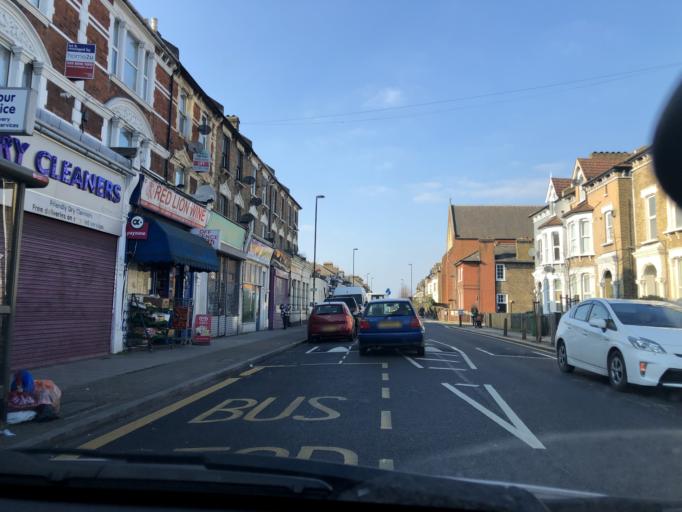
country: GB
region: England
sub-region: Greater London
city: Catford
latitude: 51.4514
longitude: -0.0066
